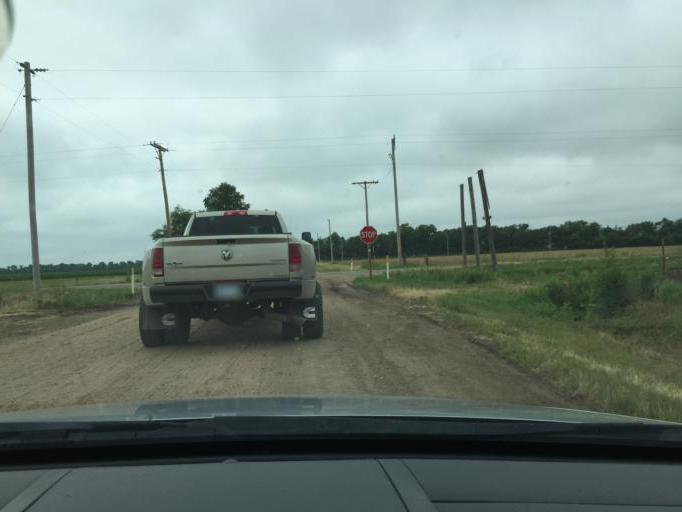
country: US
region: Kansas
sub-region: Reno County
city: South Hutchinson
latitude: 37.9704
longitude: -98.0319
